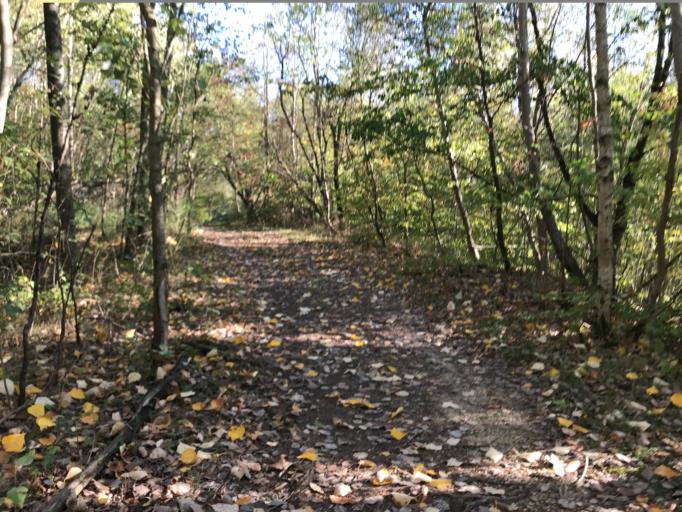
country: DE
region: Rheinland-Pfalz
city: Wolken
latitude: 50.3341
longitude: 7.4504
